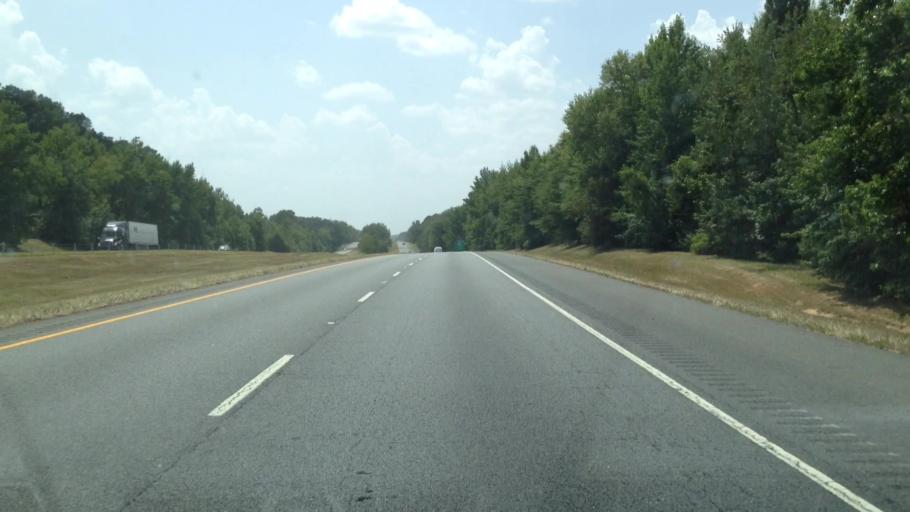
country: US
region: Louisiana
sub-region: Lincoln Parish
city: Grambling
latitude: 32.5444
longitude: -92.7414
